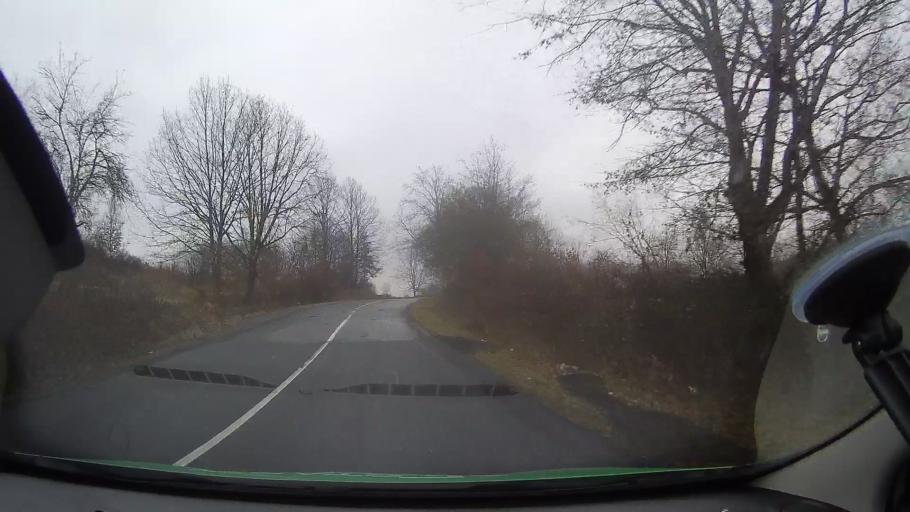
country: RO
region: Arad
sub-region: Comuna Varfurile
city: Varfurile
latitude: 46.3257
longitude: 22.4936
